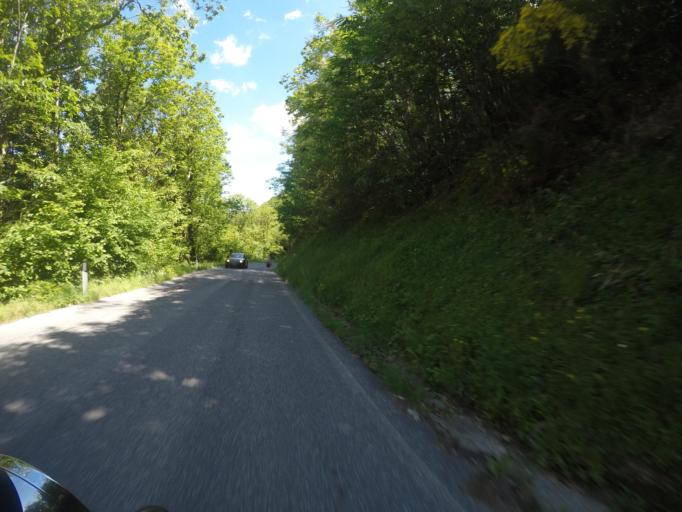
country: IT
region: Tuscany
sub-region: Provincia di Lucca
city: Careggine
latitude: 44.1313
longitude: 10.3358
